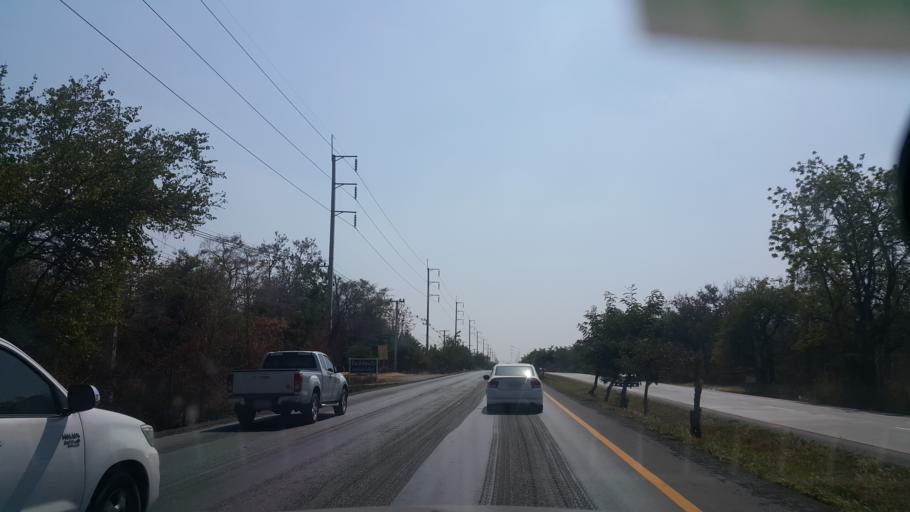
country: TH
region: Nakhon Ratchasima
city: Sida
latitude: 15.5647
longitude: 102.5524
